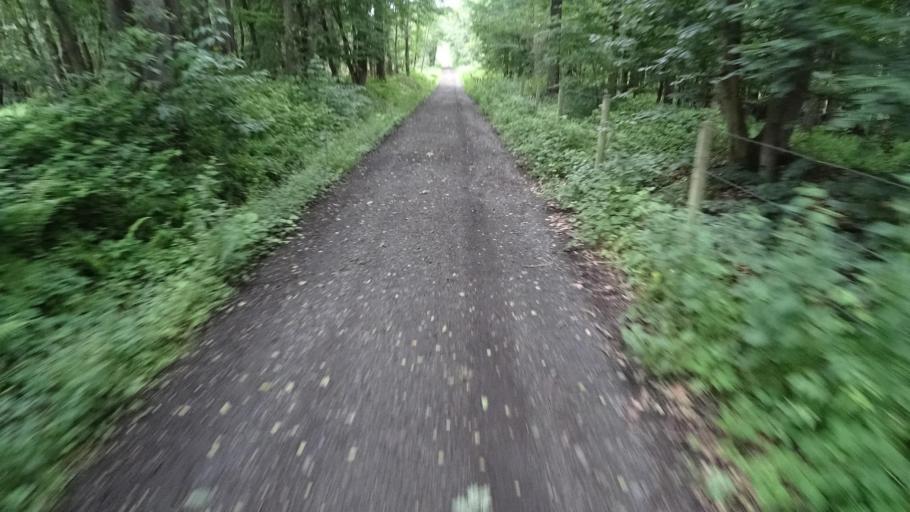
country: DE
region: Rheinland-Pfalz
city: Vettelschoss
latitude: 50.6105
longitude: 7.3284
